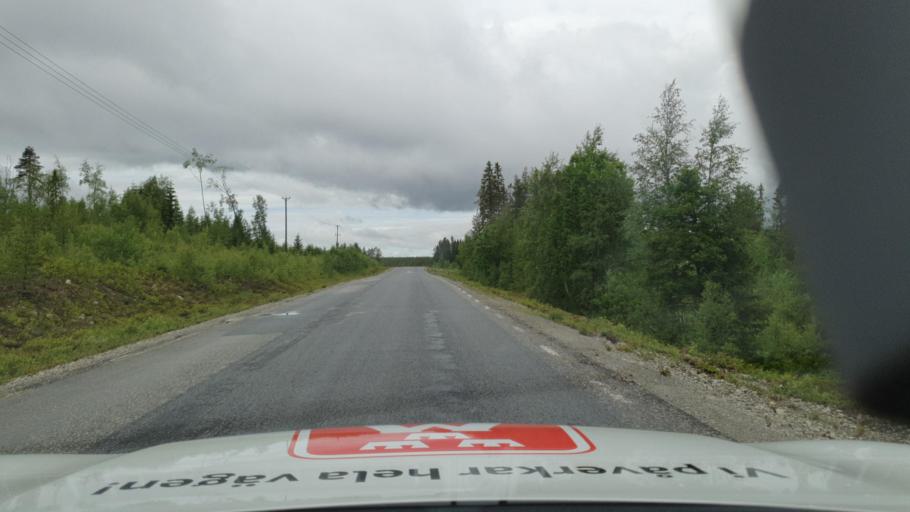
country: SE
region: Vaesterbotten
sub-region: Dorotea Kommun
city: Dorotea
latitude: 64.1791
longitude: 16.6345
